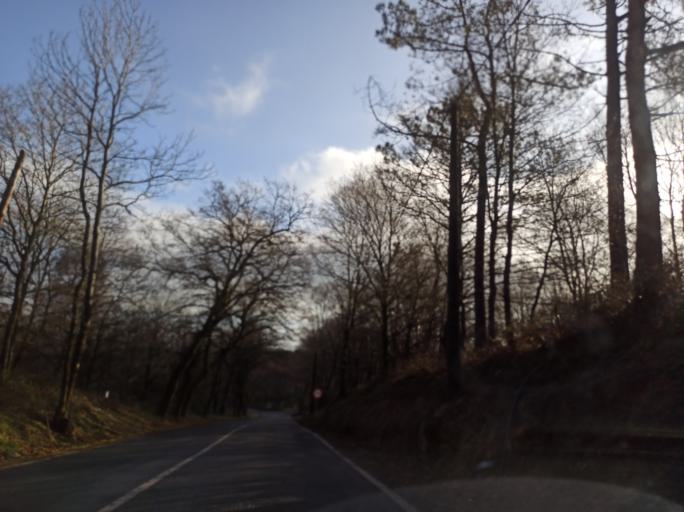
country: ES
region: Galicia
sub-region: Provincia da Coruna
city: Sobrado
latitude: 43.0786
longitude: -8.0097
